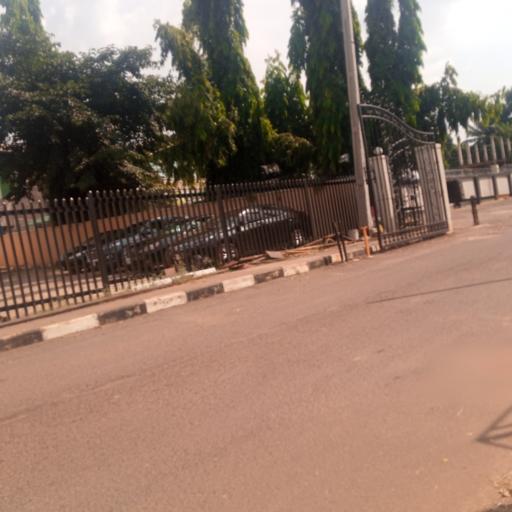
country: NG
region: Enugu
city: Enugu
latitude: 6.4477
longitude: 7.4892
